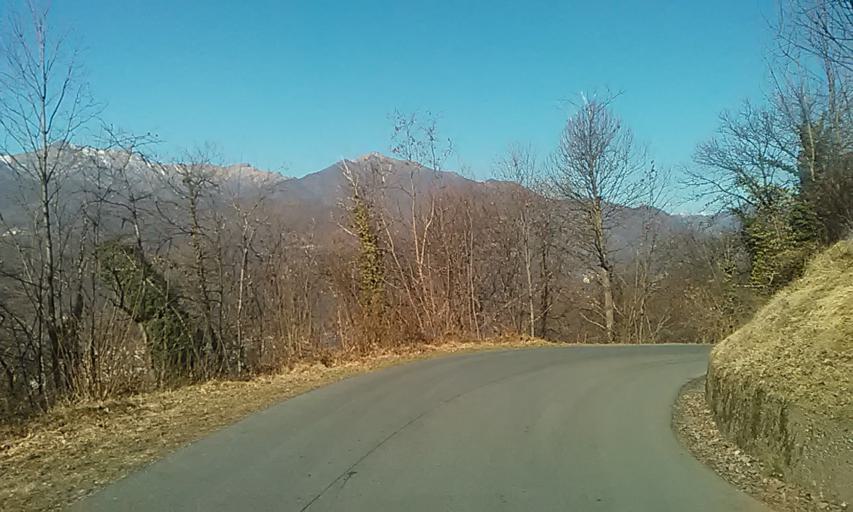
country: IT
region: Piedmont
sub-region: Provincia di Vercelli
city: Quarona
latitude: 45.7600
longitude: 8.2784
